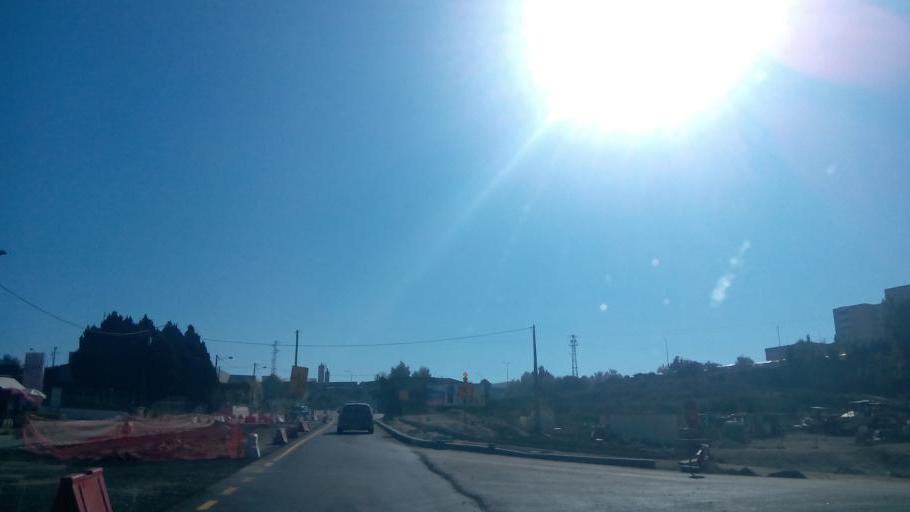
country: PT
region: Porto
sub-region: Paredes
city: Paredes
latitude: 41.1999
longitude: -8.3116
